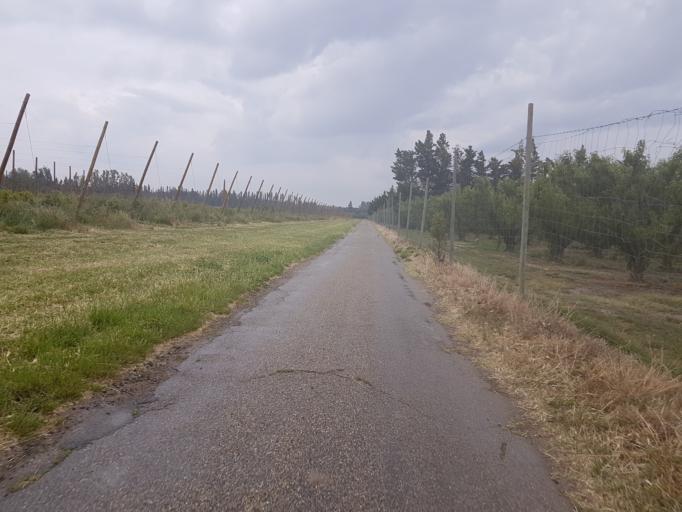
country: FR
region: Languedoc-Roussillon
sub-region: Departement du Gard
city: Villeneuve-les-Avignon
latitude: 43.9723
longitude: 4.8223
